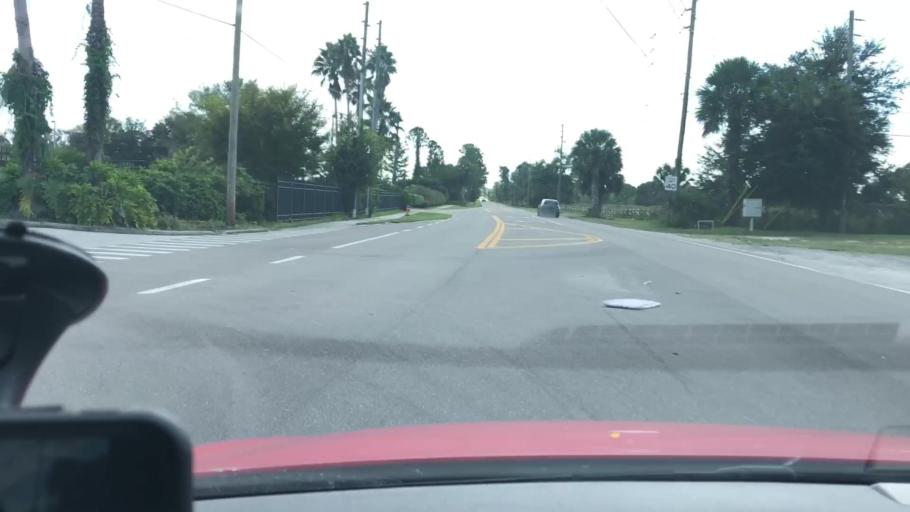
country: US
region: Florida
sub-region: Volusia County
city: North DeLand
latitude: 29.0545
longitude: -81.2812
